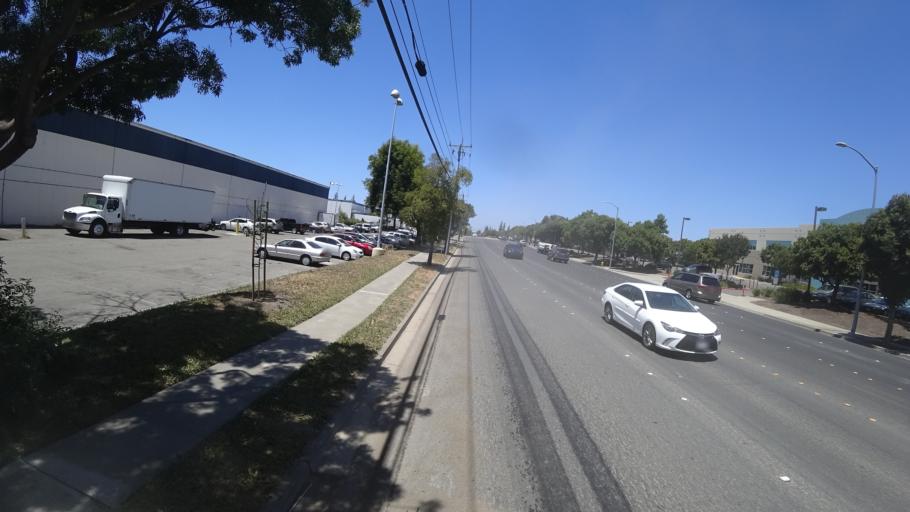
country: US
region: California
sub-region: Alameda County
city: Cherryland
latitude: 37.6362
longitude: -122.1148
